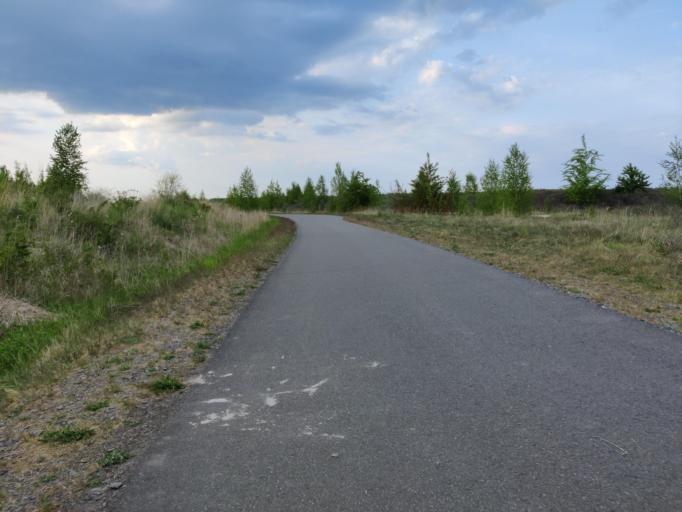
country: DE
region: Saxony
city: Rotha
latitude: 51.2395
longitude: 12.4405
